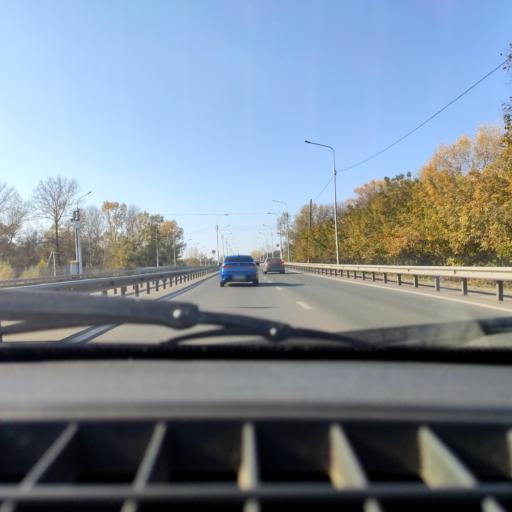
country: RU
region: Bashkortostan
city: Ufa
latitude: 54.7016
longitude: 55.9203
